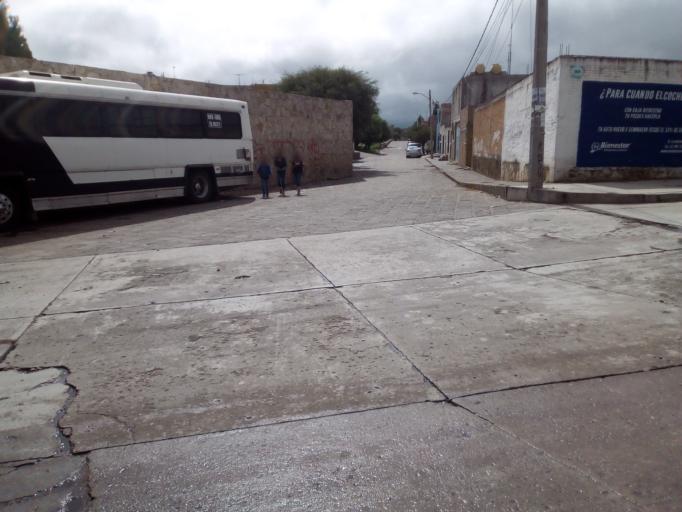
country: MX
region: Guerrero
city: San Luis de la Paz
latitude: 21.2933
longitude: -100.5105
